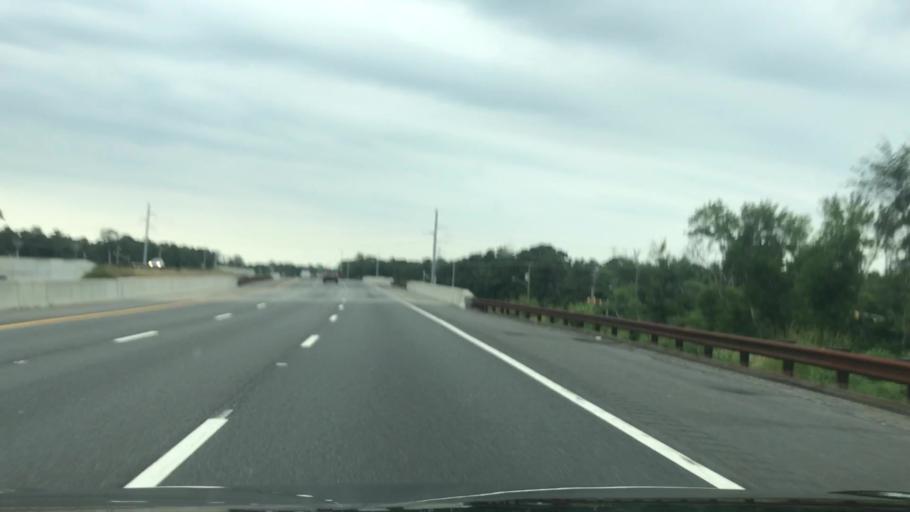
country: US
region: New Jersey
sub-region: Monmouth County
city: Ramtown
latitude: 40.0797
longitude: -74.1555
